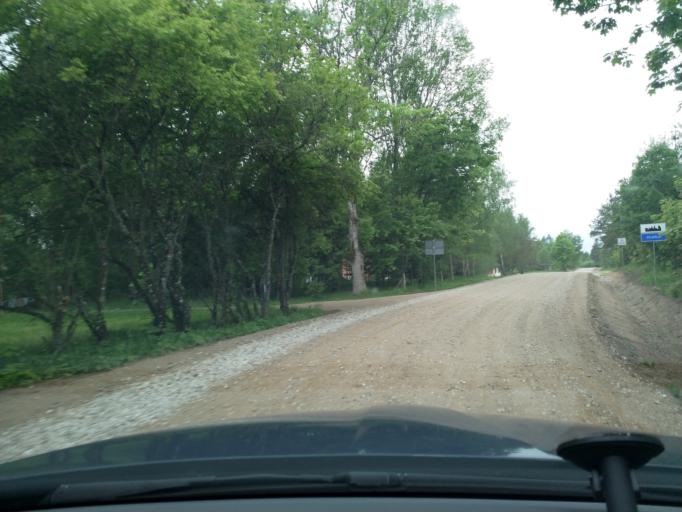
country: LV
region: Kuldigas Rajons
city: Kuldiga
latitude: 56.8818
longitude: 21.8335
